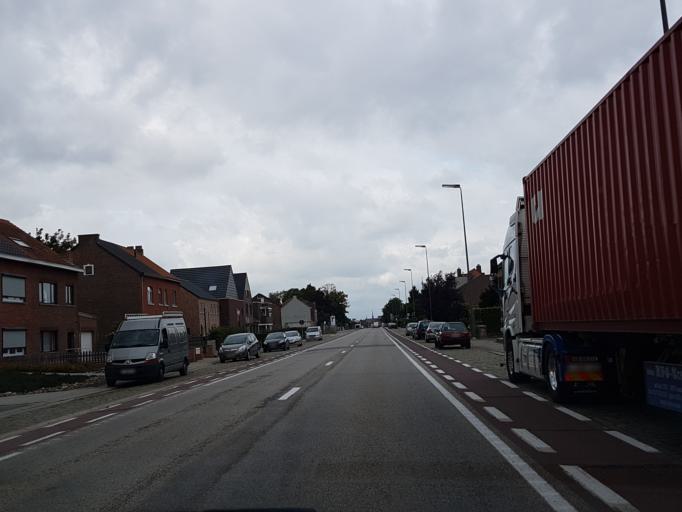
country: BE
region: Flanders
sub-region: Provincie Limburg
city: Sint-Truiden
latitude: 50.8050
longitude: 5.2007
